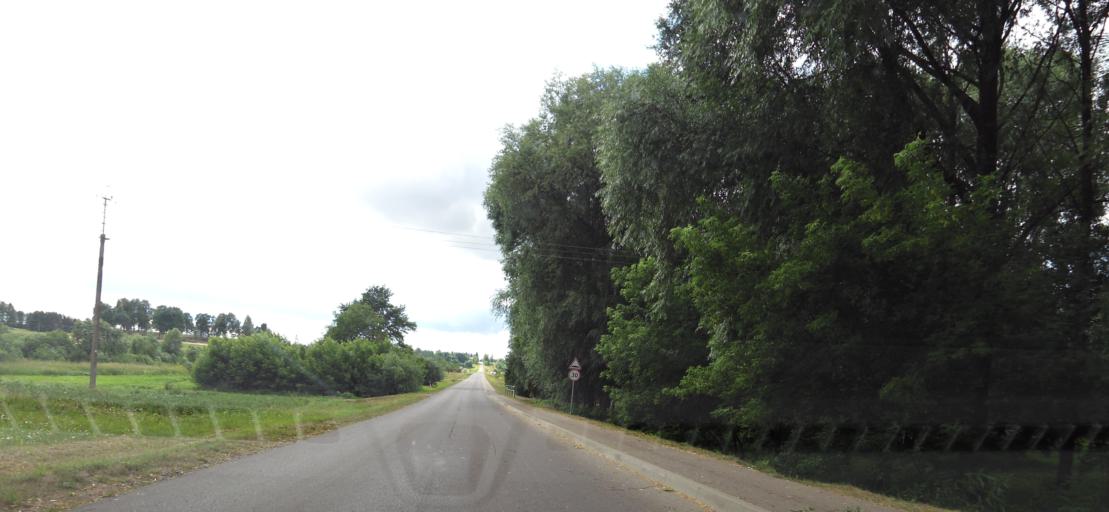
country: LT
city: Kupiskis
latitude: 55.8490
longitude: 24.9830
